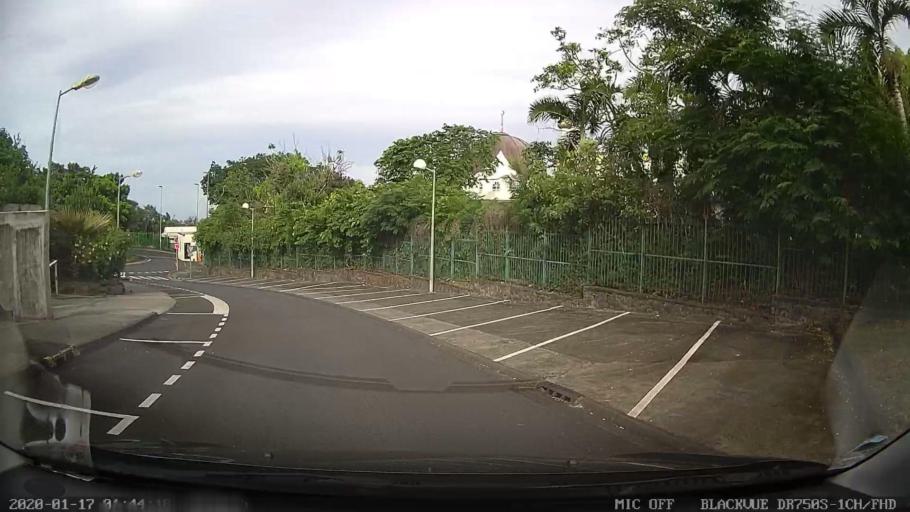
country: RE
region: Reunion
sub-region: Reunion
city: Saint-Denis
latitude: -20.9033
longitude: 55.4861
